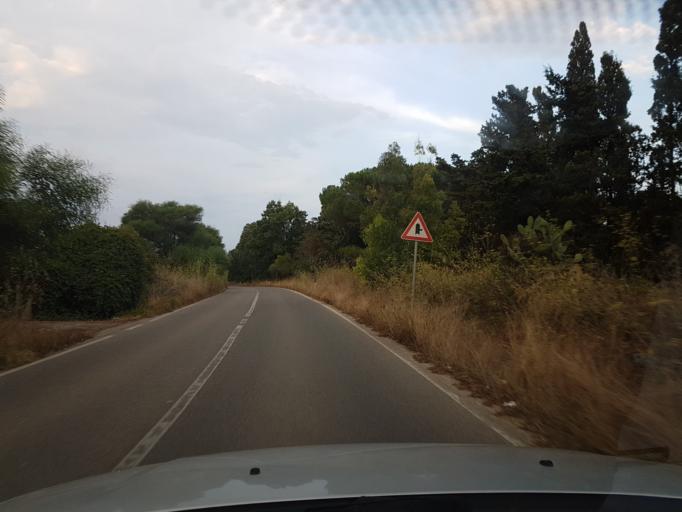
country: IT
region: Sardinia
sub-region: Provincia di Oristano
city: Solanas
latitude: 39.9311
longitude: 8.5569
